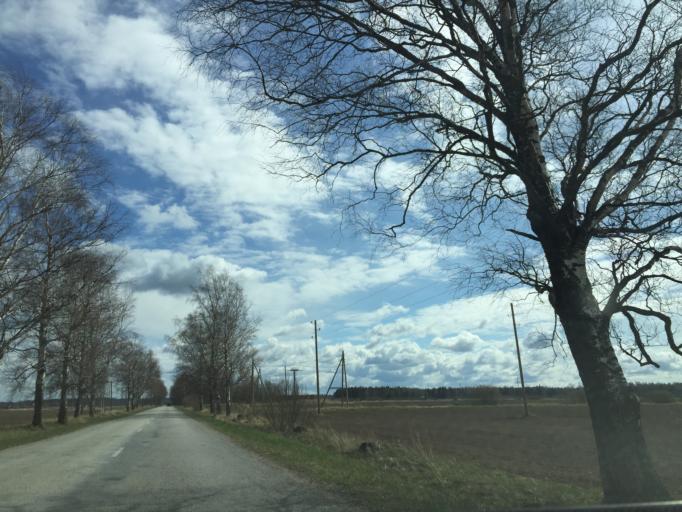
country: LV
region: Salacgrivas
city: Salacgriva
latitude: 57.7474
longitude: 24.3770
